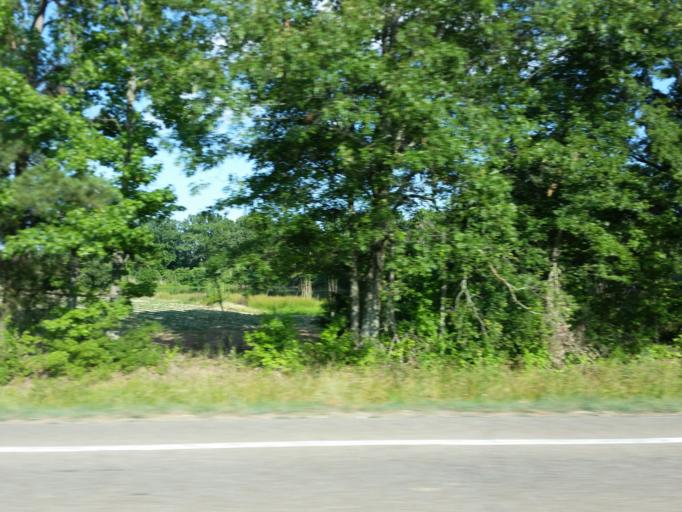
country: US
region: Mississippi
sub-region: Calhoun County
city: Calhoun City
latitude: 33.8175
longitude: -89.3438
